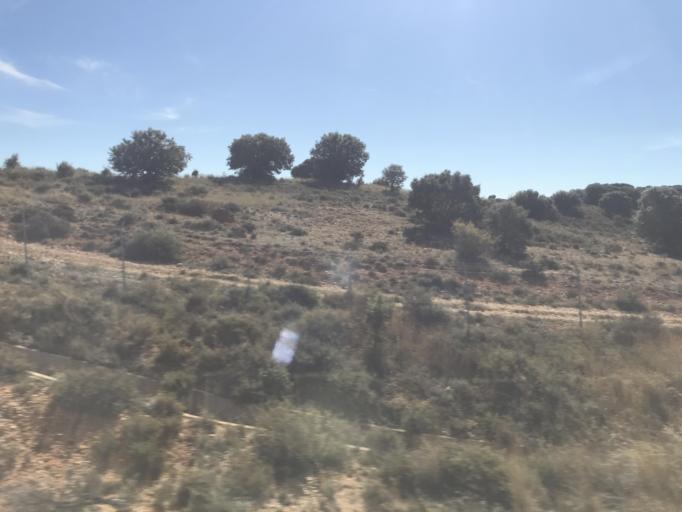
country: ES
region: Aragon
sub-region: Provincia de Zaragoza
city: Cetina
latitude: 41.2476
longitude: -1.9679
